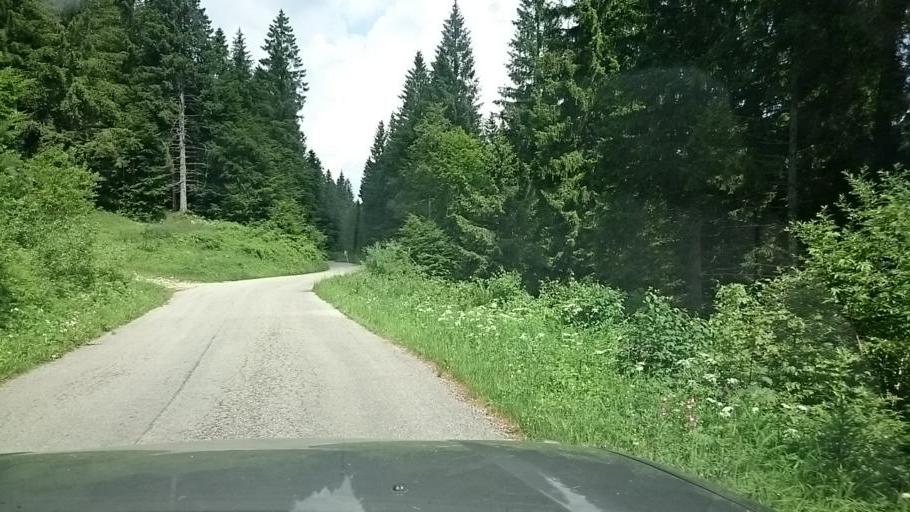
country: IT
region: Veneto
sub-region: Provincia di Vicenza
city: Foza
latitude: 45.9357
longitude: 11.6299
